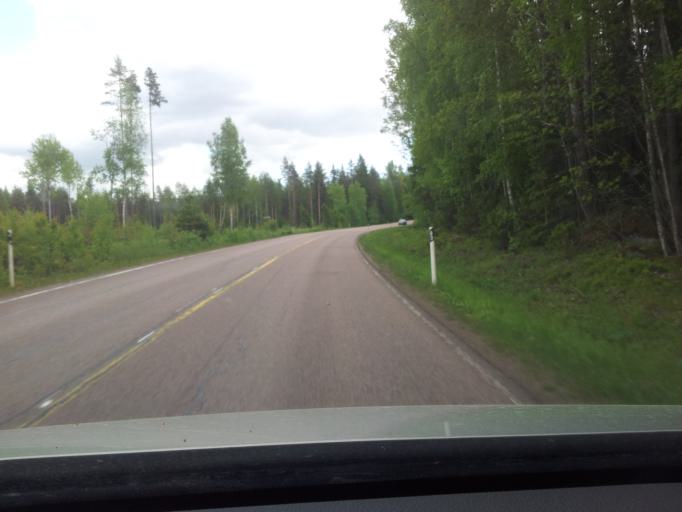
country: FI
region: South Karelia
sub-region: Lappeenranta
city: Luumaeki
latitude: 60.9772
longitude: 27.5498
